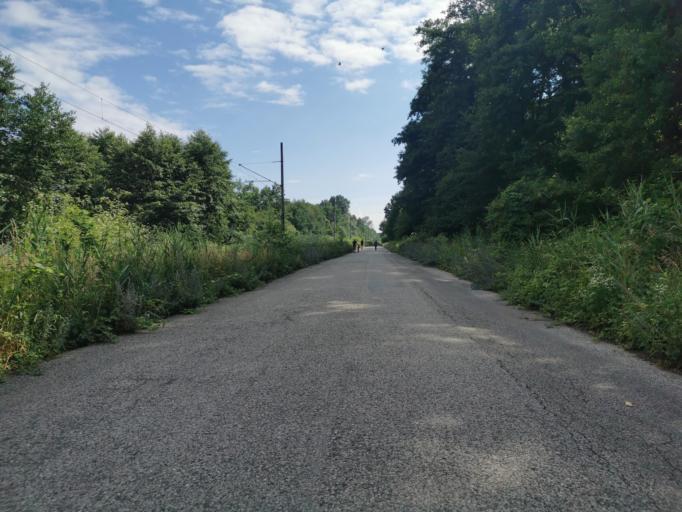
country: SK
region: Trnavsky
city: Gbely
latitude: 48.7185
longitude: 17.0878
